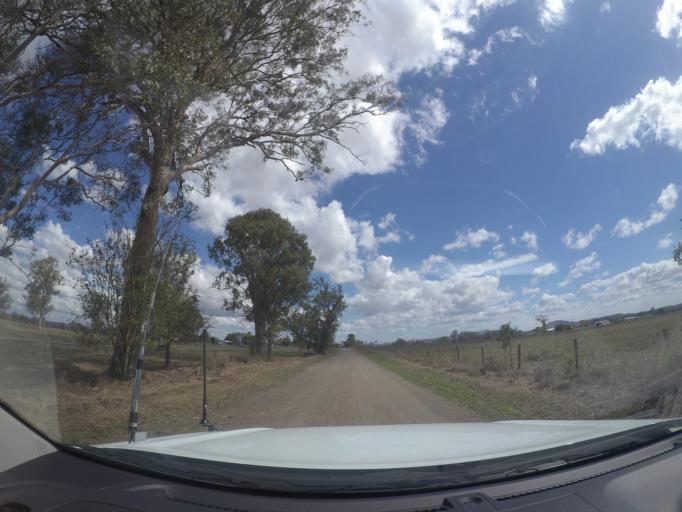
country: AU
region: Queensland
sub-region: Logan
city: Cedar Vale
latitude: -27.8946
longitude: 152.9588
